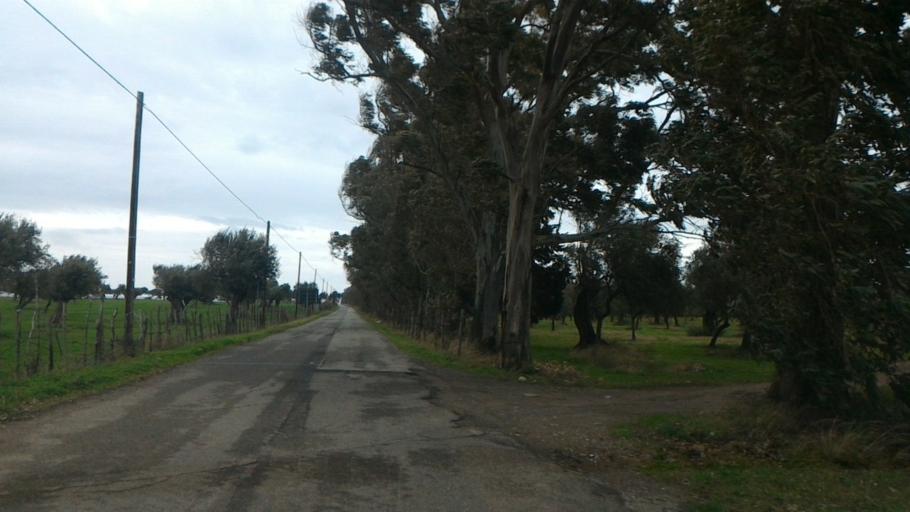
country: IT
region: Calabria
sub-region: Provincia di Crotone
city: Ciro Marina
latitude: 39.4005
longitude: 17.1170
